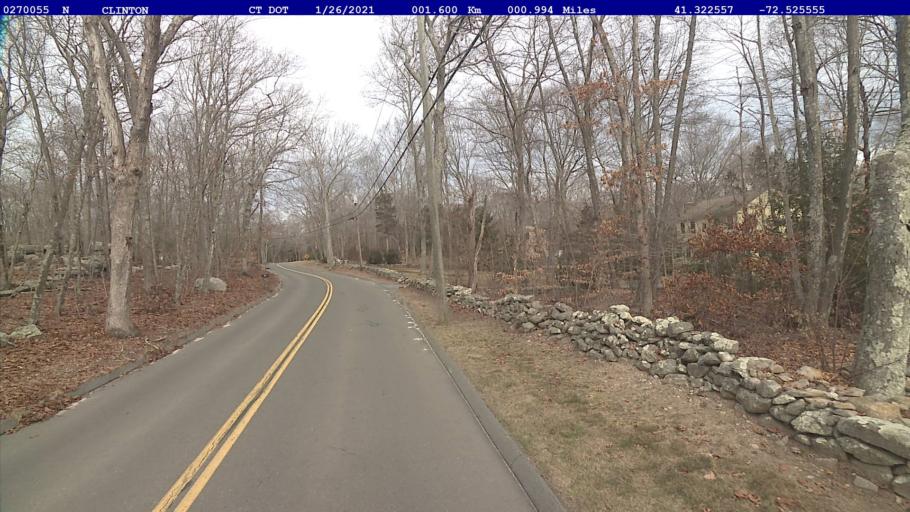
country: US
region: Connecticut
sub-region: Middlesex County
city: Clinton
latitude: 41.3226
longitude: -72.5256
